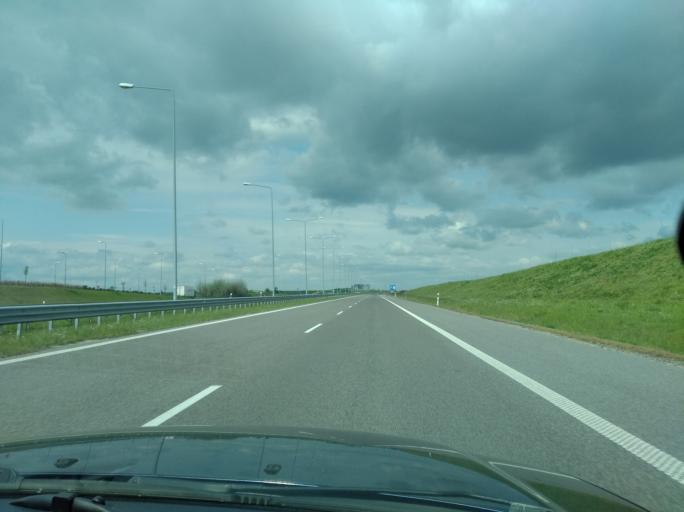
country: PL
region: Subcarpathian Voivodeship
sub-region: Powiat jaroslawski
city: Ostrow
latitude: 49.9165
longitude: 22.7650
